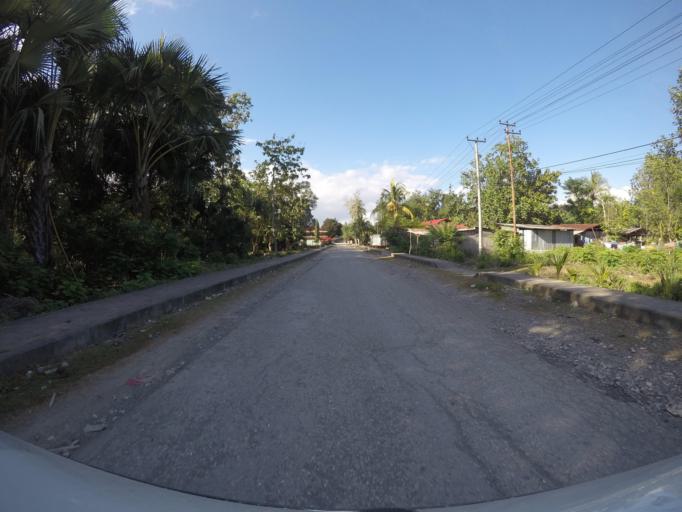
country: TL
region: Viqueque
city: Viqueque
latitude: -8.8513
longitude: 126.3659
